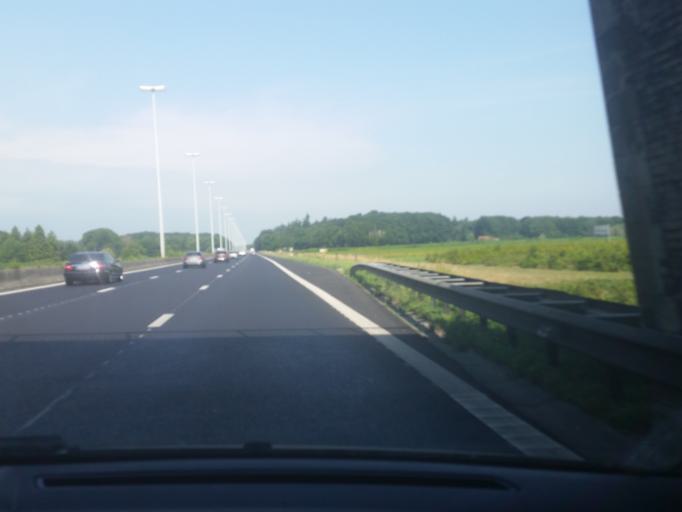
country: BE
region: Flanders
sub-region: Provincie Oost-Vlaanderen
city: Knesselare
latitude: 51.1038
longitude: 3.3781
